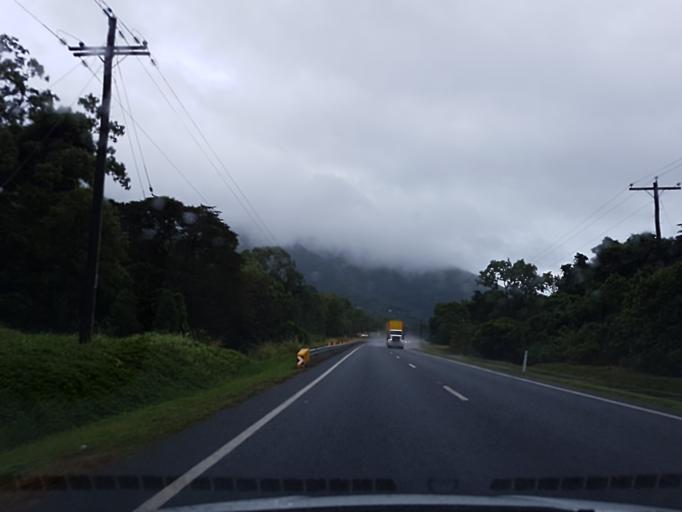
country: AU
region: Queensland
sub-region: Cairns
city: Palm Cove
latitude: -16.7611
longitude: 145.6651
